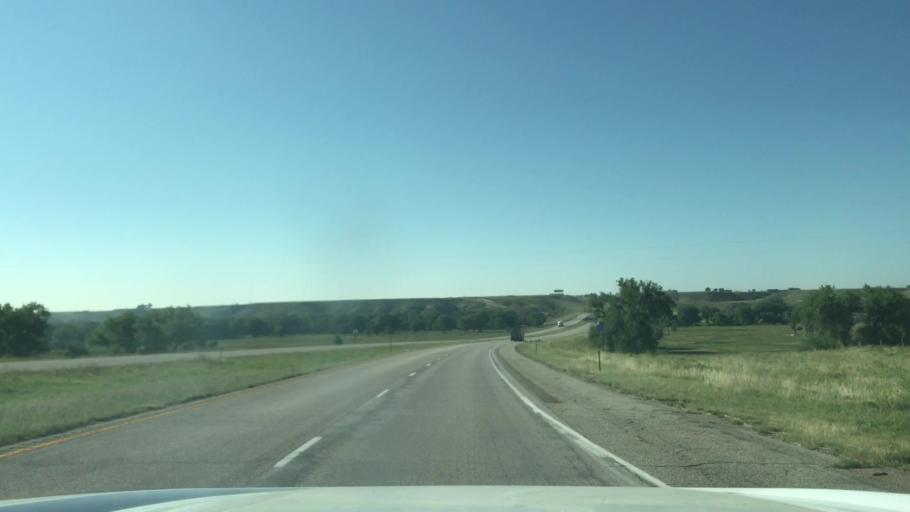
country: US
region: Wyoming
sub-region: Platte County
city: Wheatland
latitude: 42.1217
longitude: -104.9931
